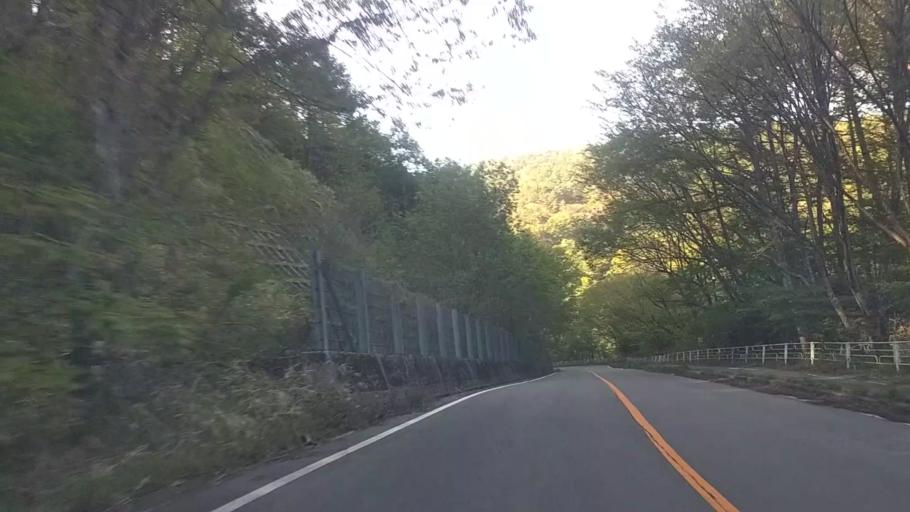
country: JP
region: Yamanashi
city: Nirasaki
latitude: 35.9050
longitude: 138.3778
